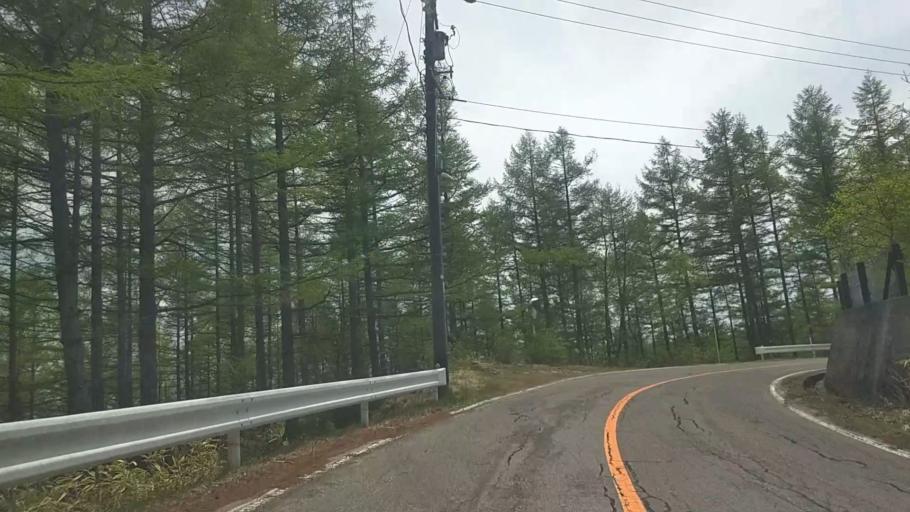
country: JP
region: Nagano
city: Saku
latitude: 36.0626
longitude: 138.3859
